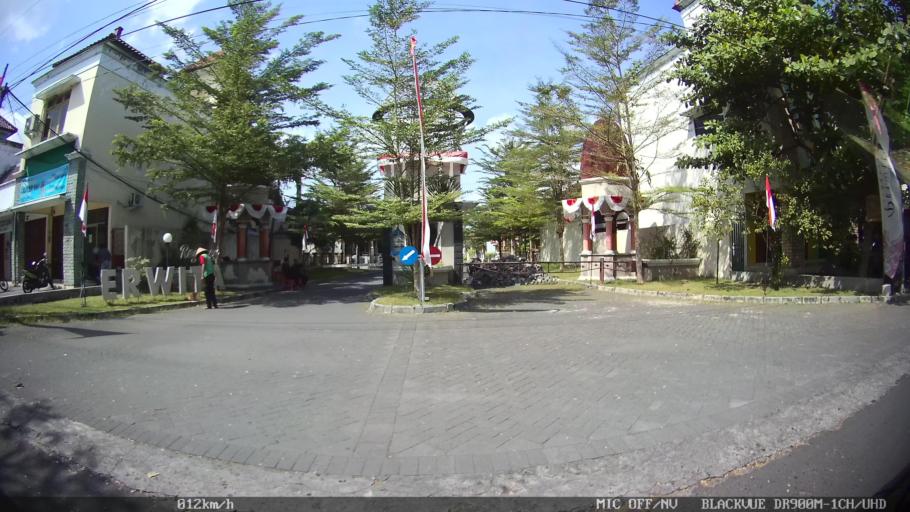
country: ID
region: Daerah Istimewa Yogyakarta
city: Kasihan
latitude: -7.8282
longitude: 110.3692
